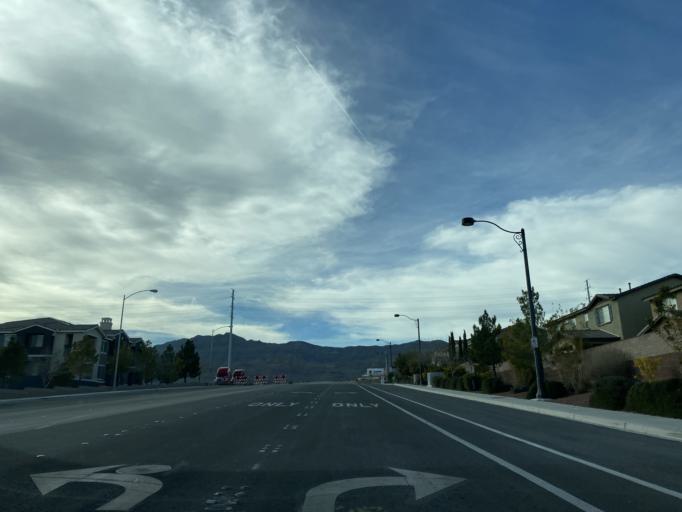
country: US
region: Nevada
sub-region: Clark County
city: Summerlin South
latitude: 36.2772
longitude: -115.3312
